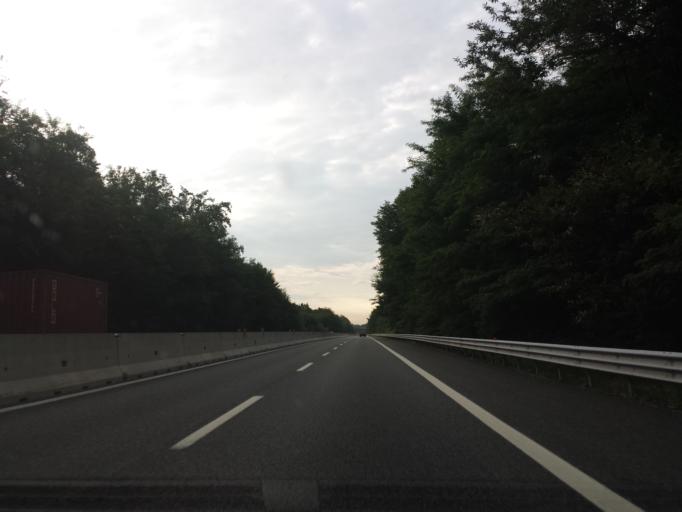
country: IT
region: Lombardy
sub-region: Provincia di Varese
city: Arsago Seprio
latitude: 45.7014
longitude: 8.7393
